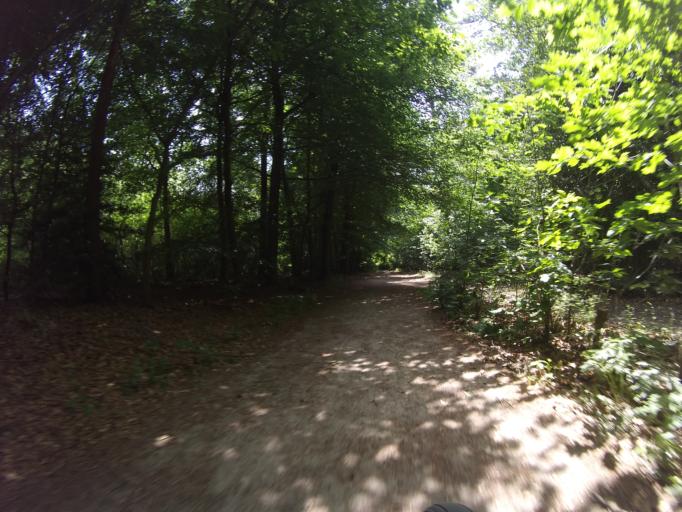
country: NL
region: Gelderland
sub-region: Gemeente Ede
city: Lunteren
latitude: 52.0831
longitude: 5.6455
